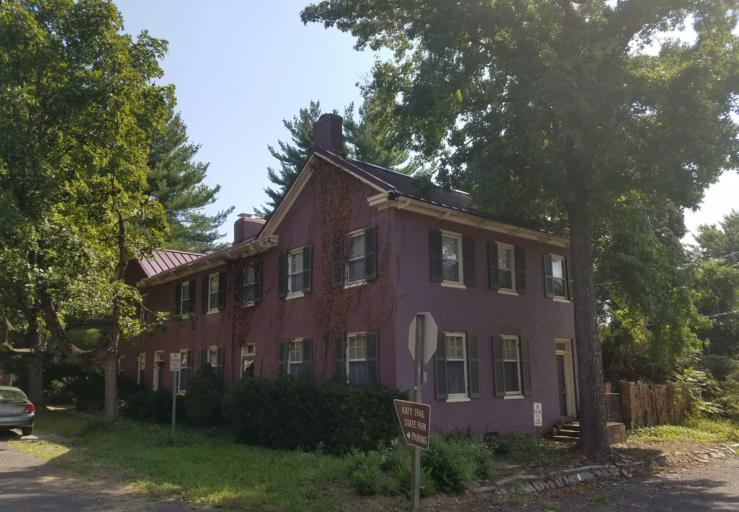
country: US
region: Missouri
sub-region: Howard County
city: New Franklin
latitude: 38.9791
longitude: -92.5665
